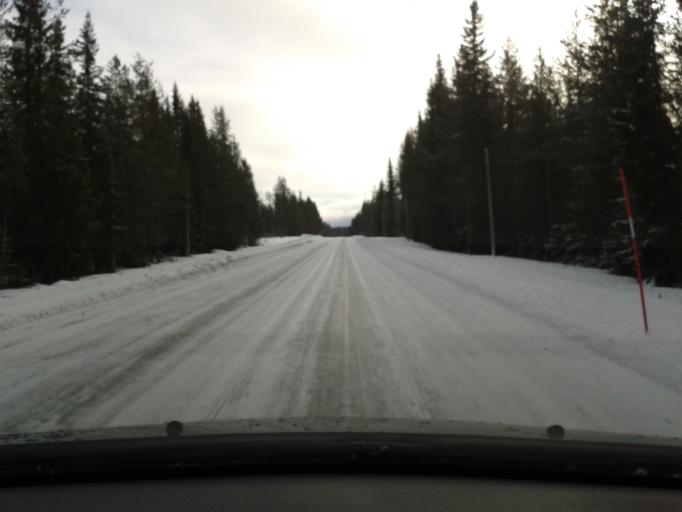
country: SE
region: Vaesterbotten
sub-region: Vilhelmina Kommun
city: Sjoberg
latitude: 64.7121
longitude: 16.2445
